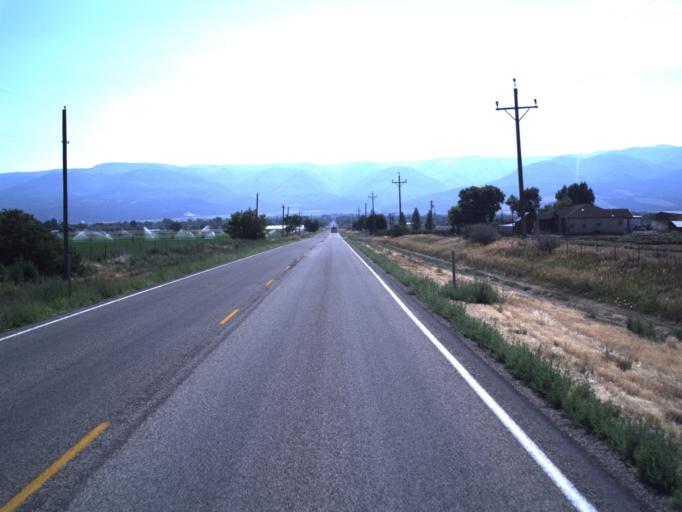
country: US
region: Utah
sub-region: Sanpete County
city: Mount Pleasant
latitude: 39.5467
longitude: -111.4928
